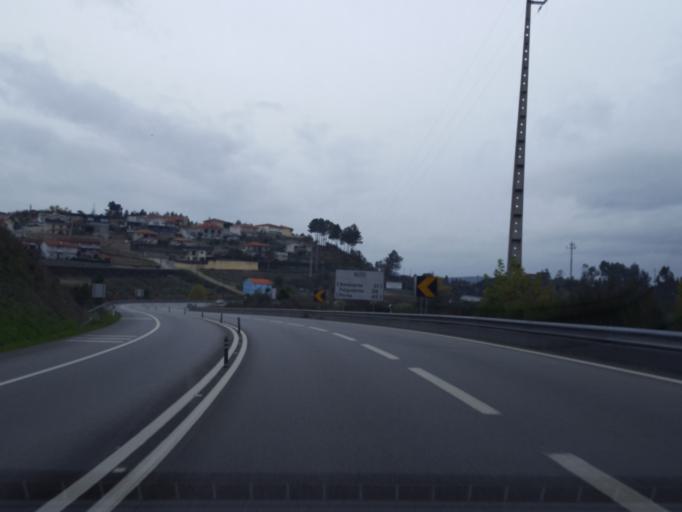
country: PT
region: Porto
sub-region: Marco de Canaveses
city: Marco de Canavezes
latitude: 41.2113
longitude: -8.1662
